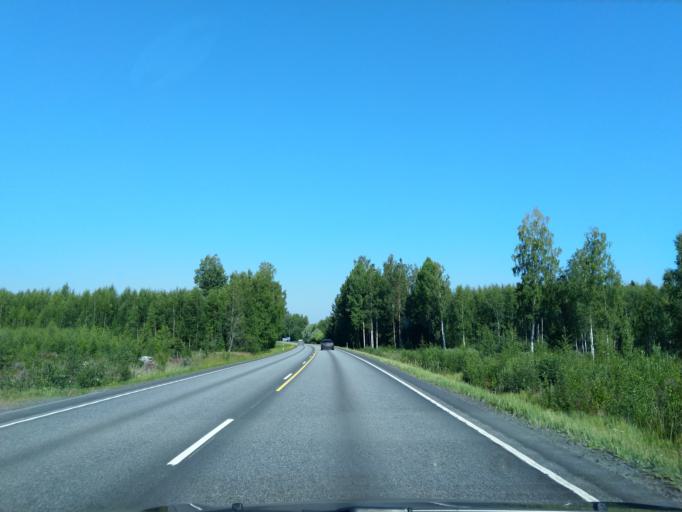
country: FI
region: Satakunta
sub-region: Pori
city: Huittinen
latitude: 61.1624
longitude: 22.7175
